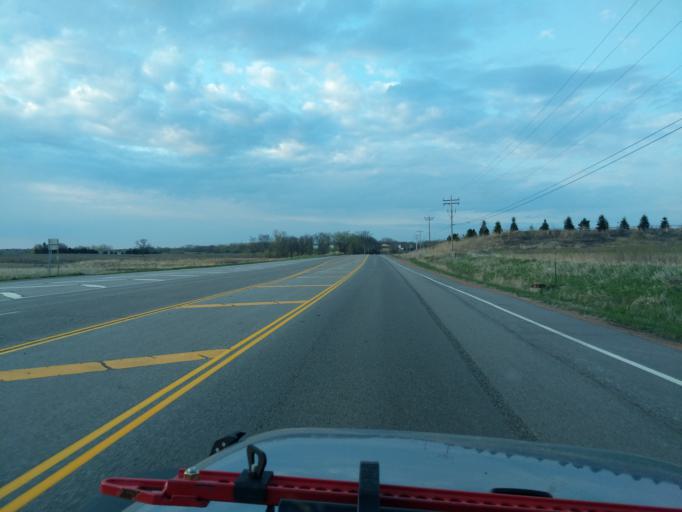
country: US
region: Minnesota
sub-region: Hennepin County
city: Rogers
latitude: 45.1822
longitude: -93.5235
